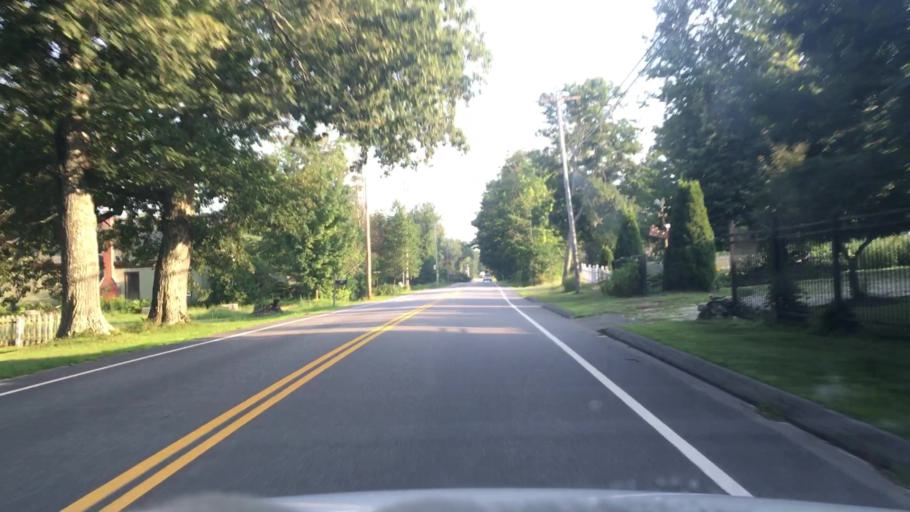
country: US
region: Maine
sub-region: Cumberland County
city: Freeport
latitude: 43.8876
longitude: -70.0938
